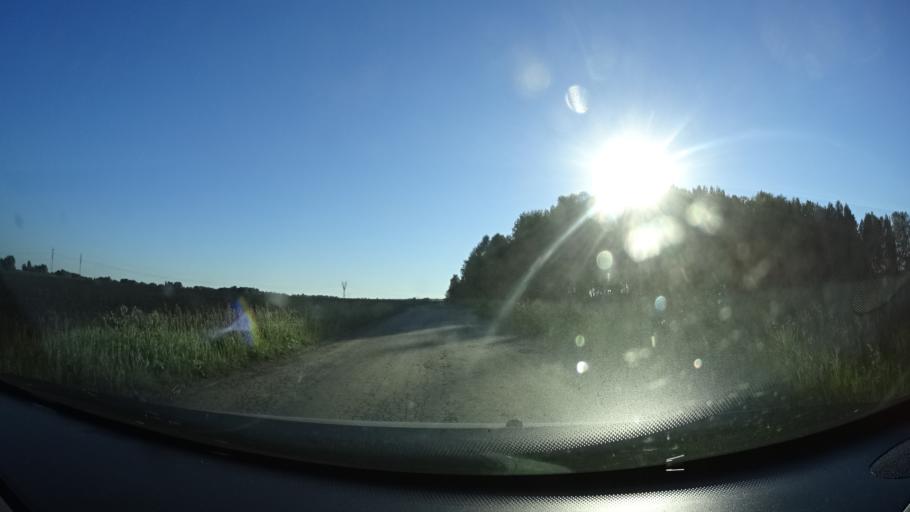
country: RU
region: Sverdlovsk
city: Achit
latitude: 56.8943
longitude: 57.5988
